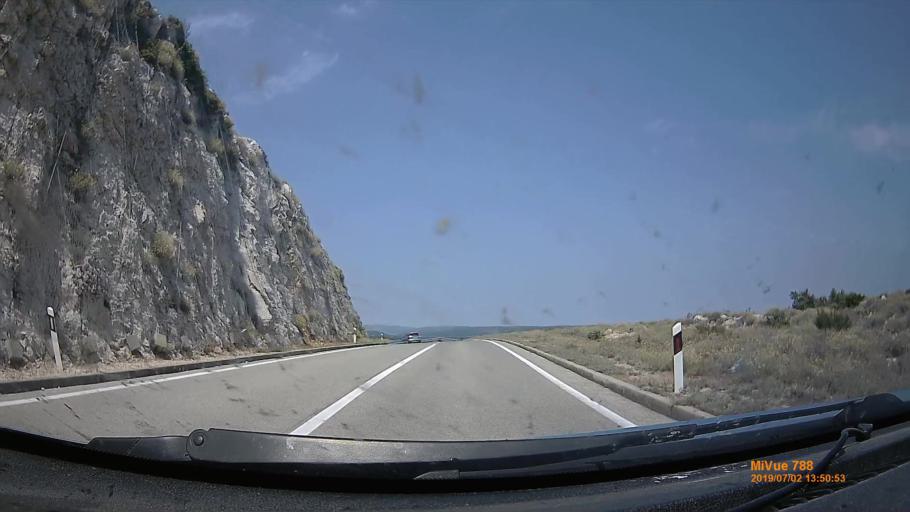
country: HR
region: Primorsko-Goranska
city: Mali Losinj
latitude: 44.6001
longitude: 14.4064
